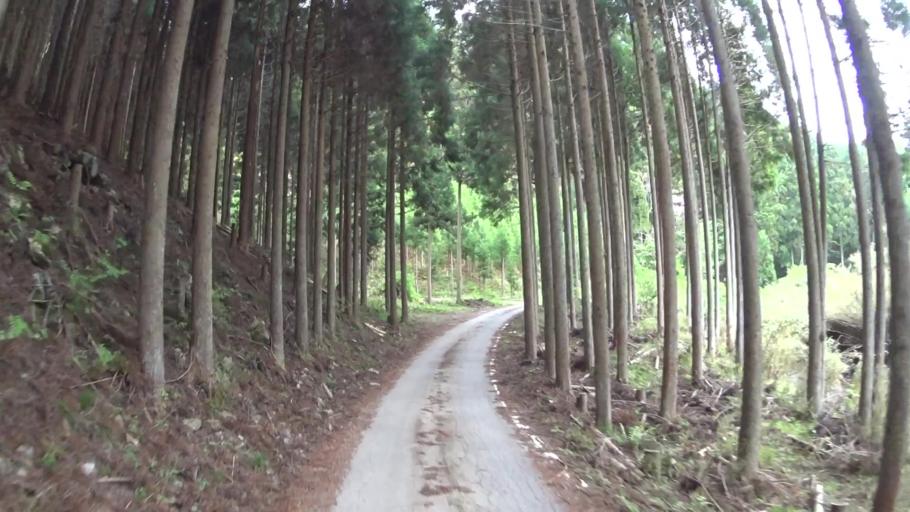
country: JP
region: Kyoto
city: Kameoka
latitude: 35.1170
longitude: 135.6305
